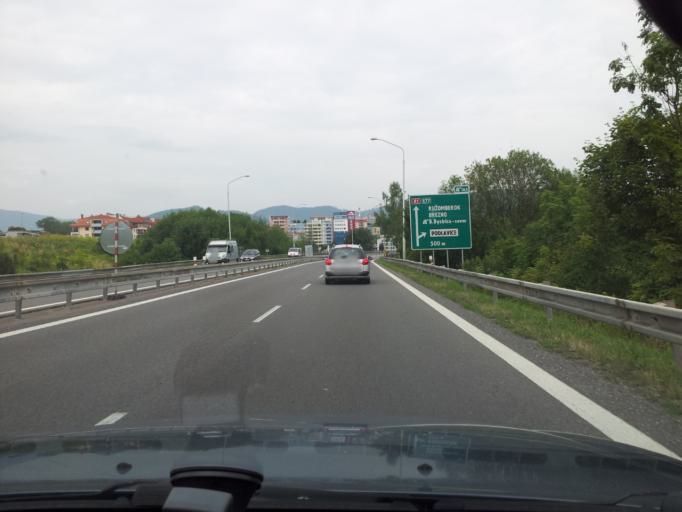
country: SK
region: Banskobystricky
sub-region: Okres Banska Bystrica
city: Banska Bystrica
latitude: 48.7351
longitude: 19.1344
